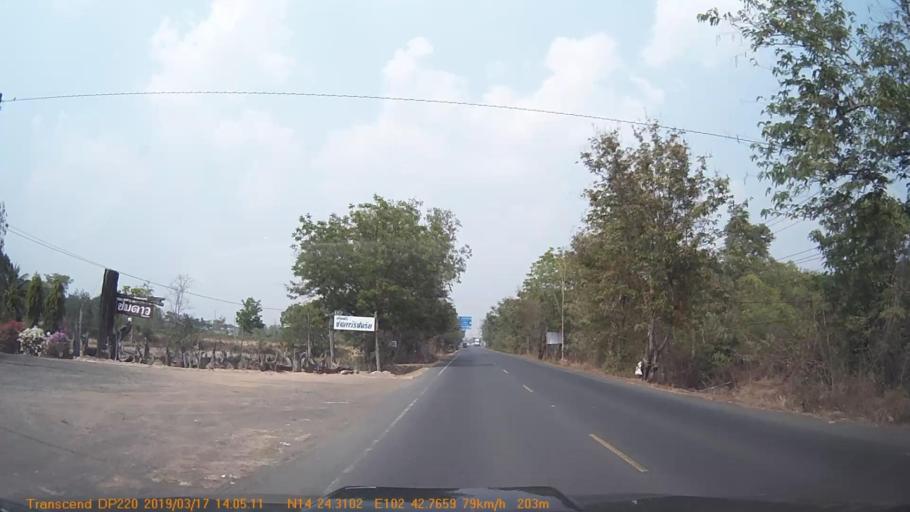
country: TH
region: Buriram
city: Pa Kham
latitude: 14.4056
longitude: 102.7129
